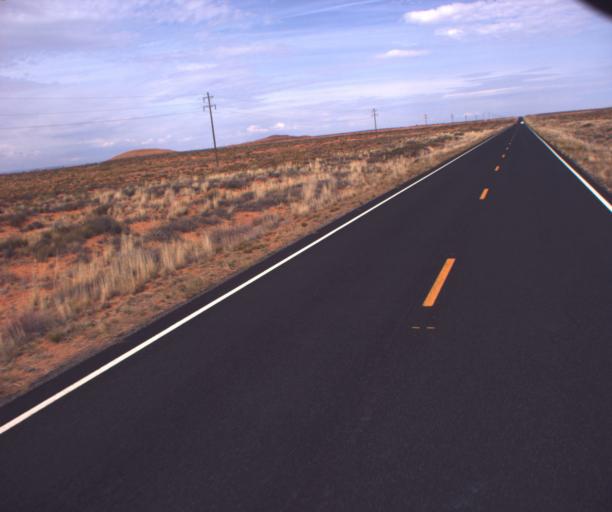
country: US
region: Arizona
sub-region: Apache County
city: Many Farms
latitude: 36.8433
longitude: -109.6407
